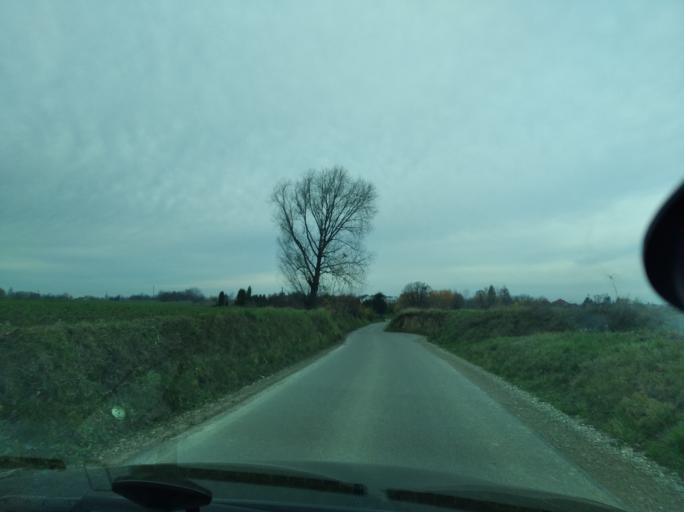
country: PL
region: Subcarpathian Voivodeship
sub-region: Powiat przeworski
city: Grzeska
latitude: 50.0698
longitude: 22.4597
